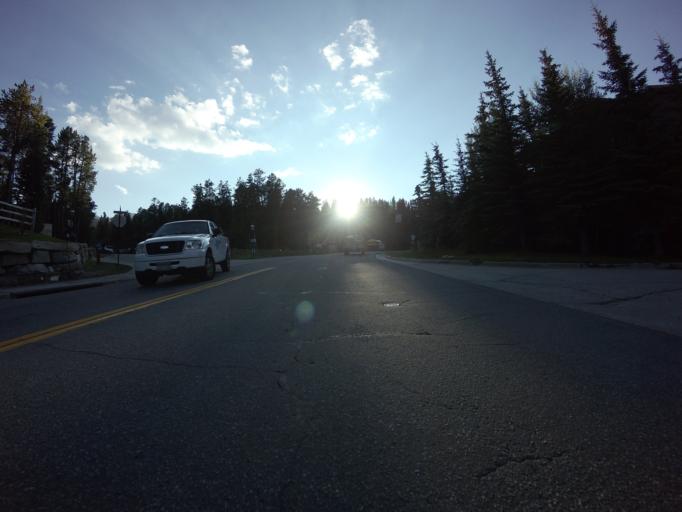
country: US
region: Colorado
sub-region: Summit County
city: Breckenridge
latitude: 39.4820
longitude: -106.0501
